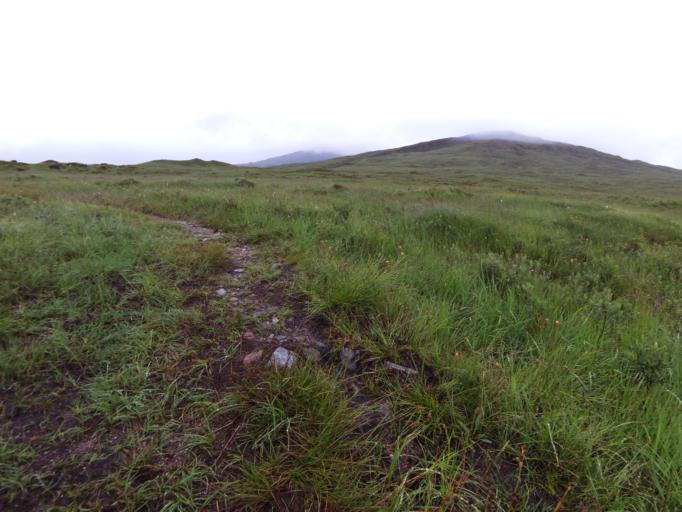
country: GB
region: Scotland
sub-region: Highland
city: Spean Bridge
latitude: 56.7694
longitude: -4.7061
